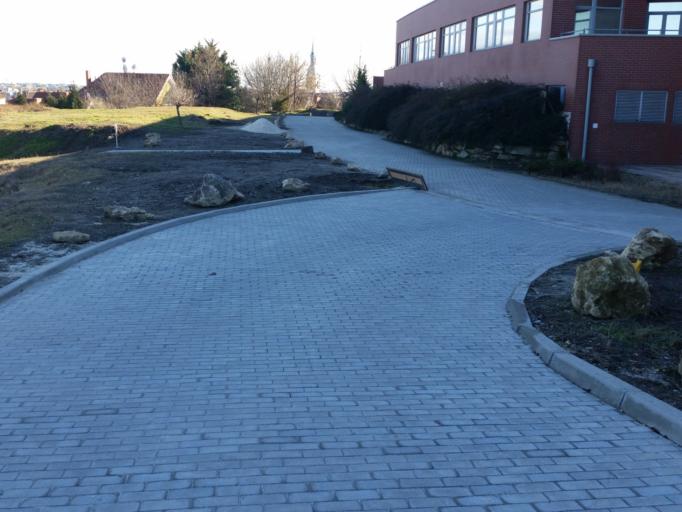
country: HU
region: Budapest
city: Budapest III. keruelet
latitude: 47.5308
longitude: 19.0351
